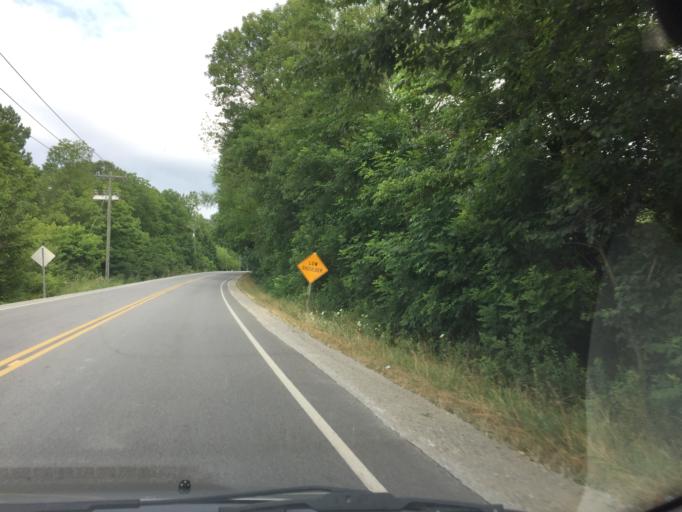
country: US
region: Tennessee
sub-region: Hamilton County
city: Apison
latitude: 34.9880
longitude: -85.0658
